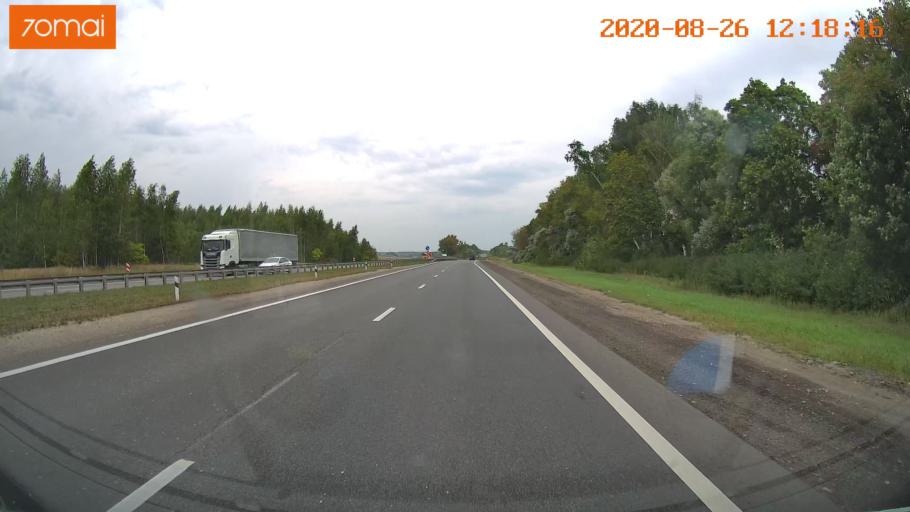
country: RU
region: Rjazan
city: Murmino
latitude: 54.4712
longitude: 40.0206
